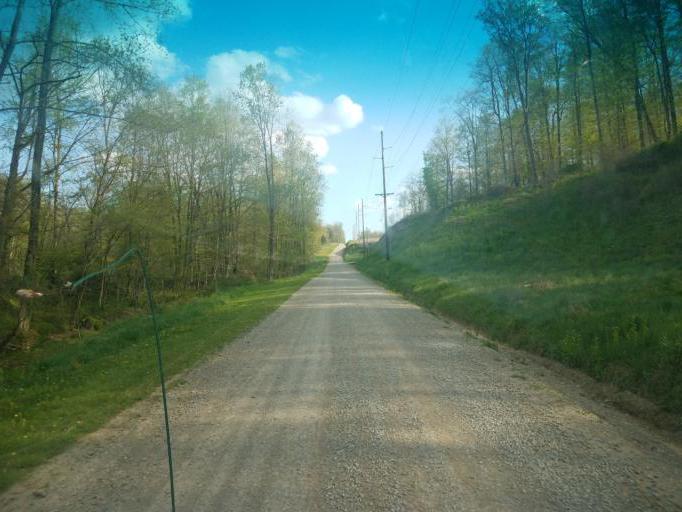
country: US
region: Ohio
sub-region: Wayne County
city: Shreve
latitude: 40.6551
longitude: -82.0336
